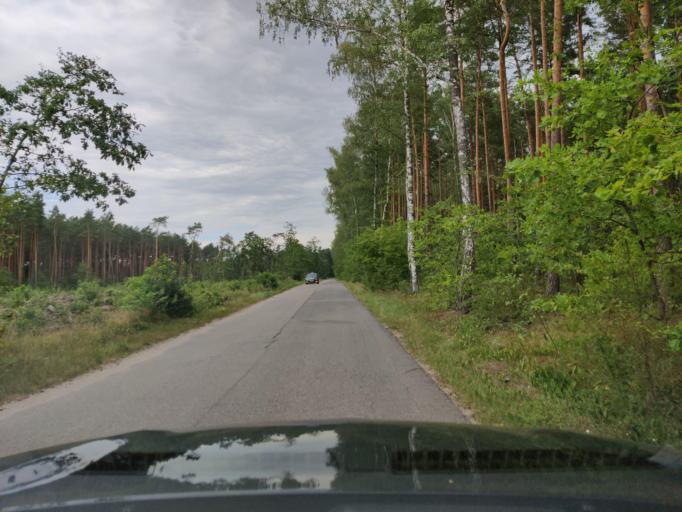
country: PL
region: Masovian Voivodeship
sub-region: Powiat pultuski
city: Pultusk
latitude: 52.7311
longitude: 21.1375
